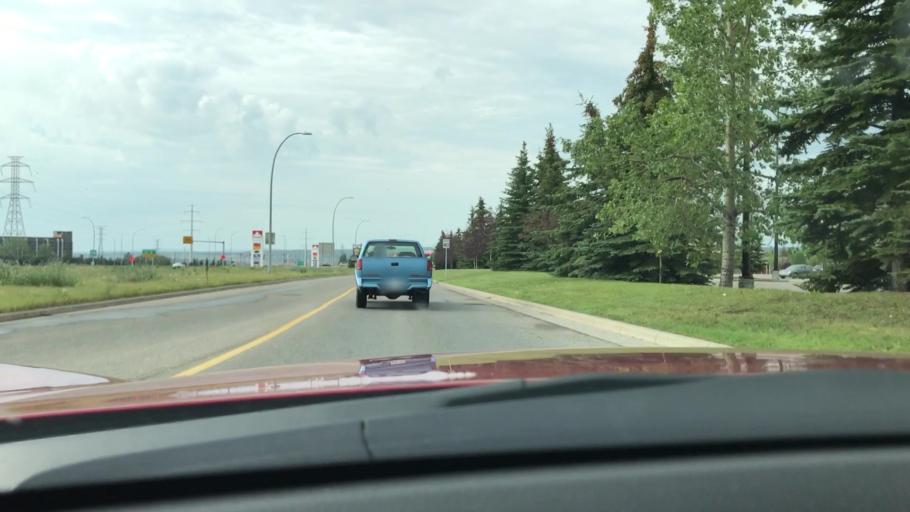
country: CA
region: Alberta
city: Calgary
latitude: 51.0217
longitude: -114.1664
